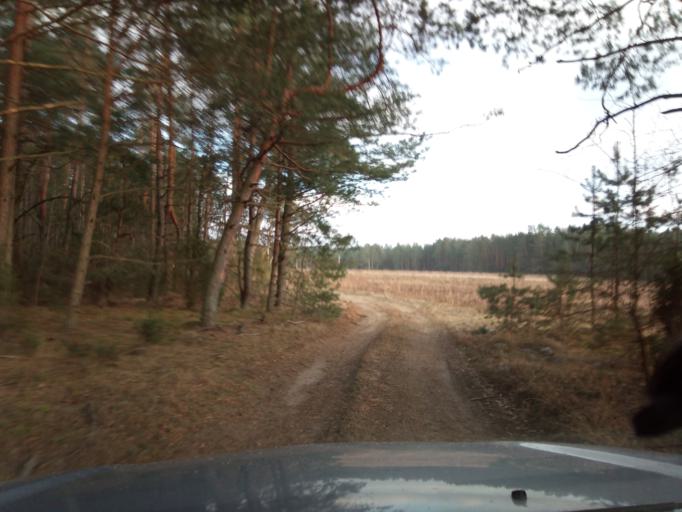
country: LT
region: Alytaus apskritis
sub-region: Alytaus rajonas
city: Daugai
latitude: 54.1031
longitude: 24.2926
